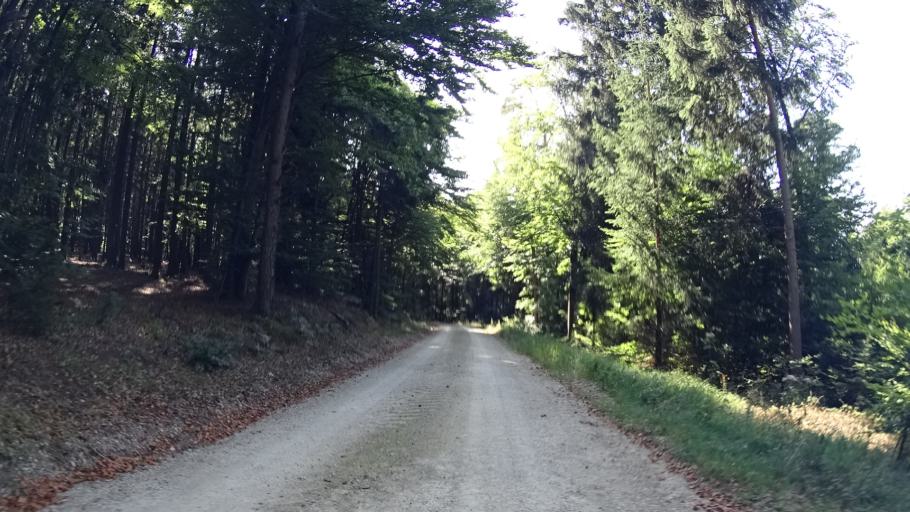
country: DE
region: Bavaria
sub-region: Upper Bavaria
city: Walting
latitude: 48.9735
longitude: 11.3447
